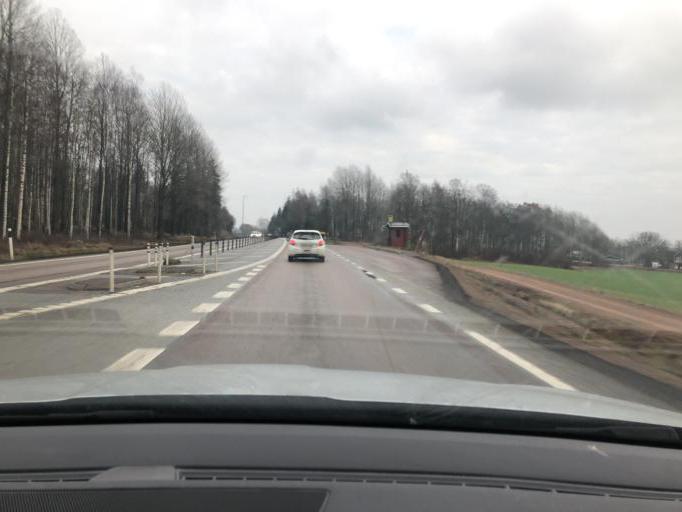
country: SE
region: Vaermland
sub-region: Kristinehamns Kommun
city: Kristinehamn
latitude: 59.3739
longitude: 13.9496
